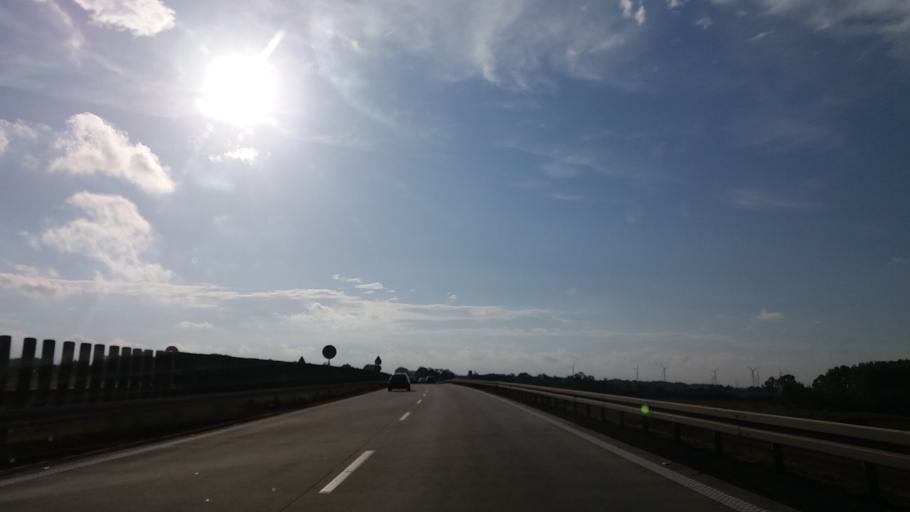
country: PL
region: Lower Silesian Voivodeship
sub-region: Powiat legnicki
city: Legnickie Pole
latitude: 51.1276
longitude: 16.3511
